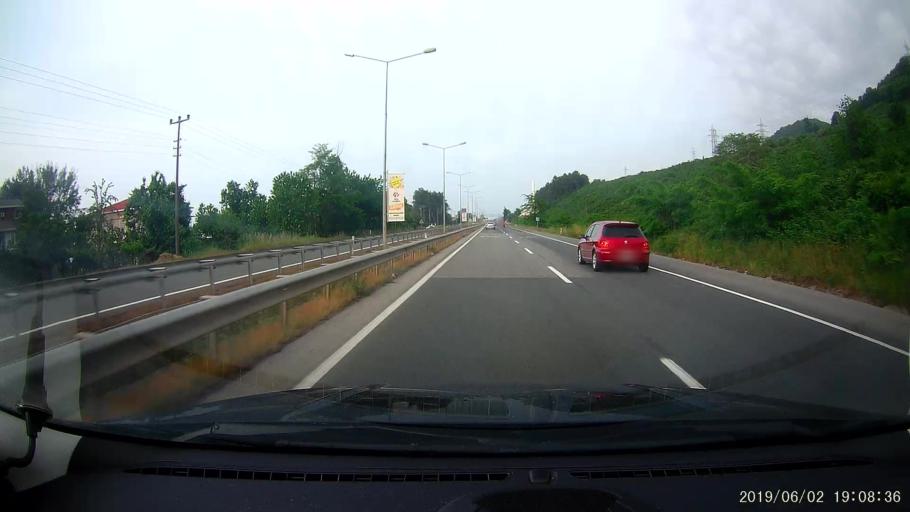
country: TR
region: Ordu
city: Gulyali
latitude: 40.9762
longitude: 38.0124
